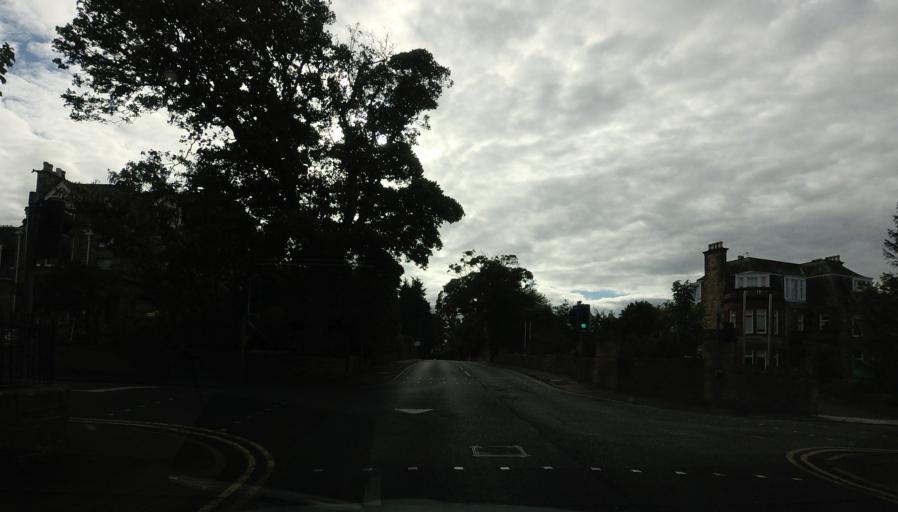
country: GB
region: Scotland
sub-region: East Lothian
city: North Berwick
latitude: 56.0572
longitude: -2.7384
